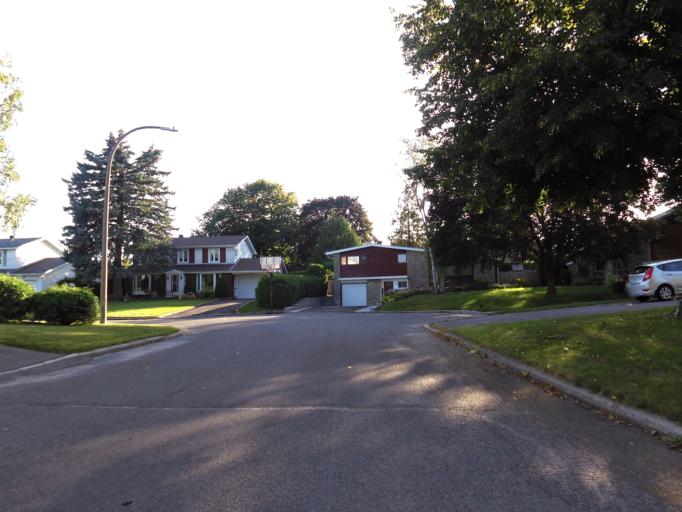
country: CA
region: Ontario
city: Ottawa
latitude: 45.3549
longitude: -75.7232
